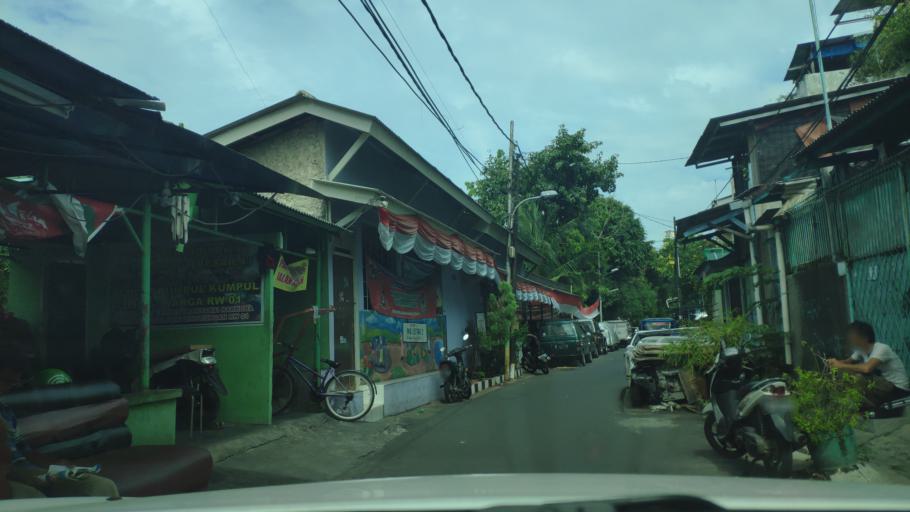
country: ID
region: Jakarta Raya
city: Jakarta
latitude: -6.1401
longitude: 106.8191
